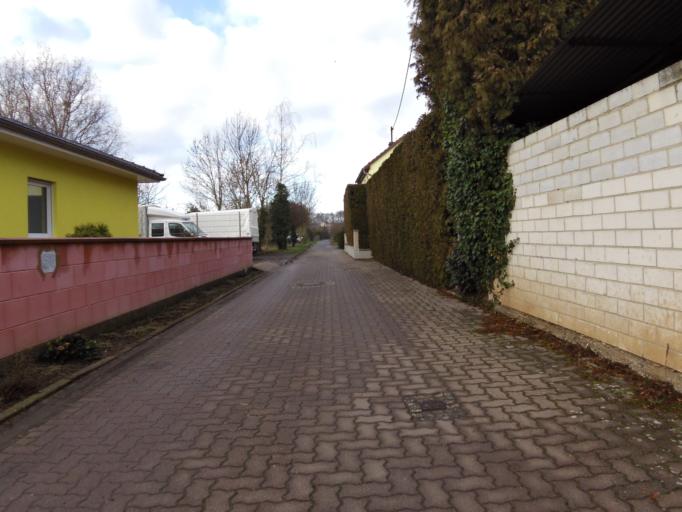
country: DE
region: Rheinland-Pfalz
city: Offstein
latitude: 49.6050
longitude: 8.2366
